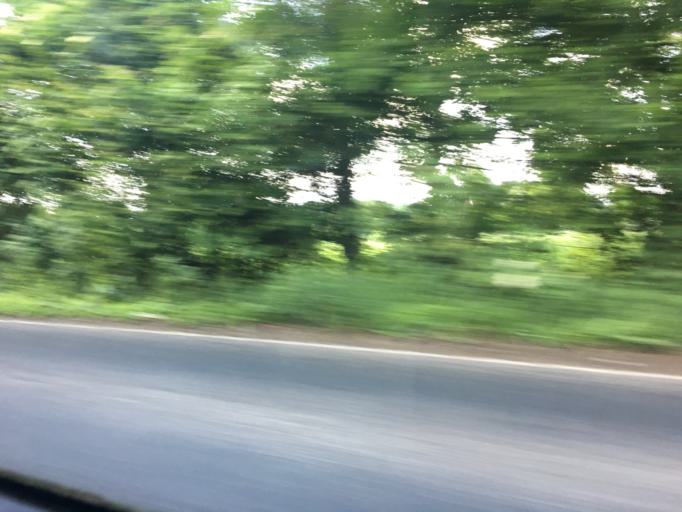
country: GB
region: England
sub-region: Leicestershire
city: Oadby
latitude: 52.6115
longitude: -1.0669
